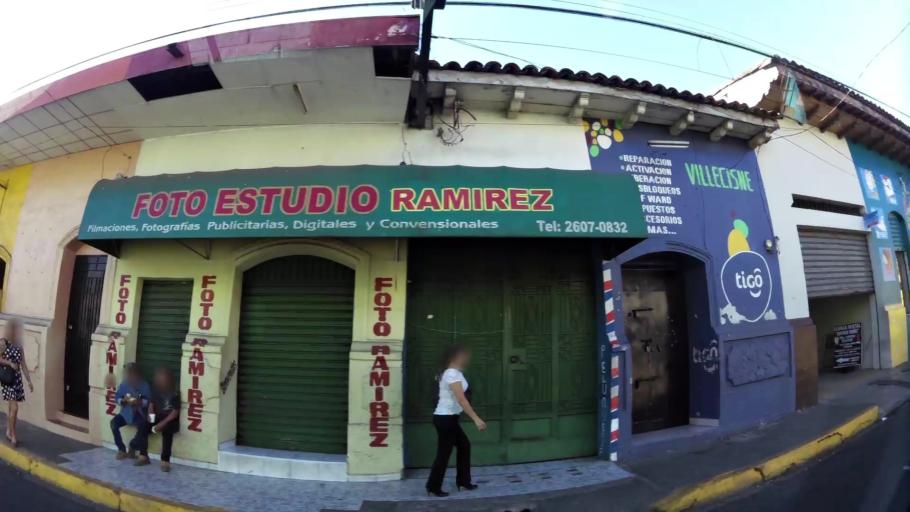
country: SV
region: San Miguel
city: San Miguel
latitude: 13.4833
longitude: -88.1731
